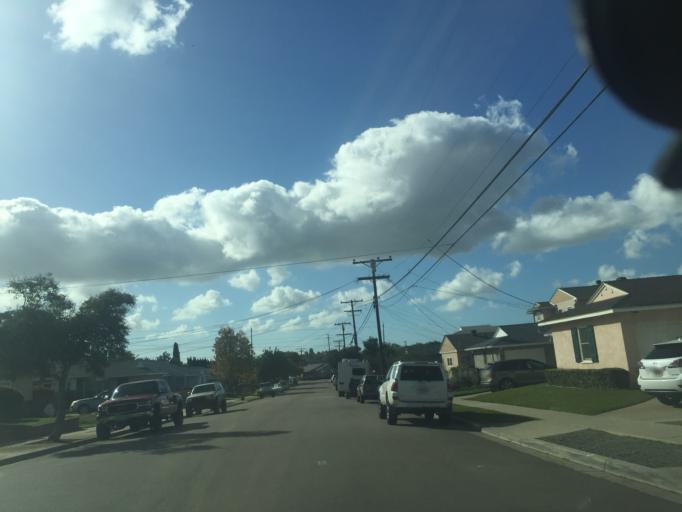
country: US
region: California
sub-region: San Diego County
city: La Mesa
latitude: 32.7898
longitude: -117.0889
